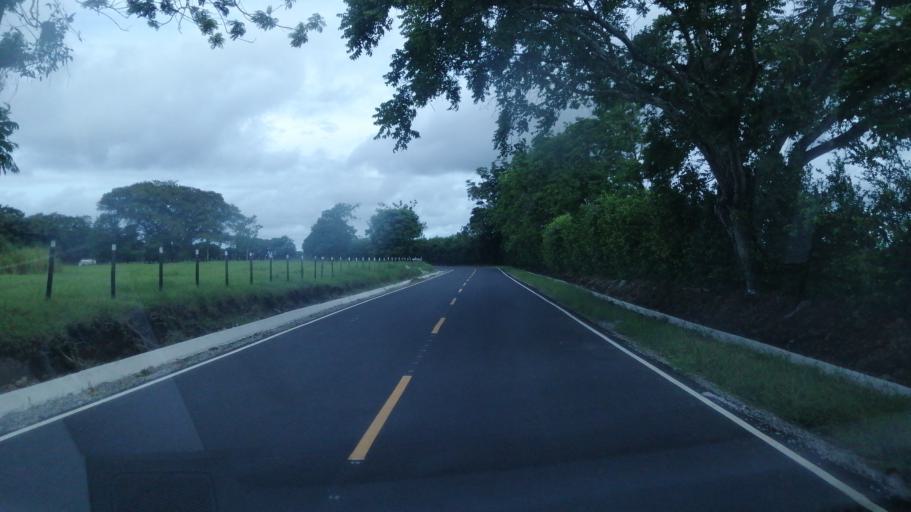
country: PA
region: Chiriqui
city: Alanje
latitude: 8.4331
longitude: -82.5197
